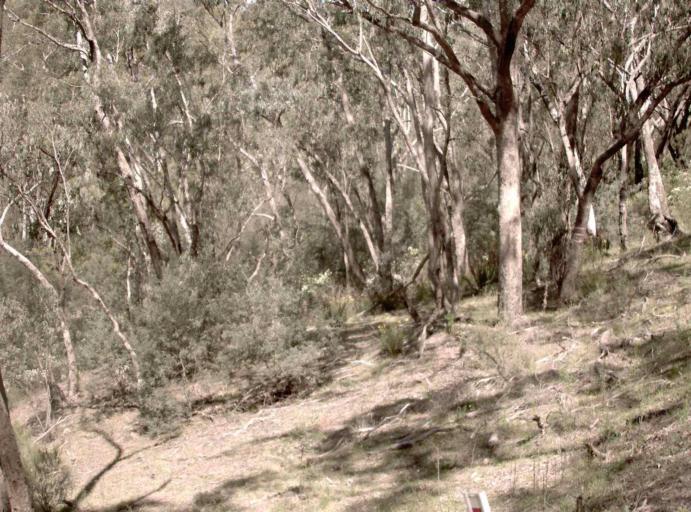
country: AU
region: New South Wales
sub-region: Bombala
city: Bombala
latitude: -37.1089
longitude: 148.6409
